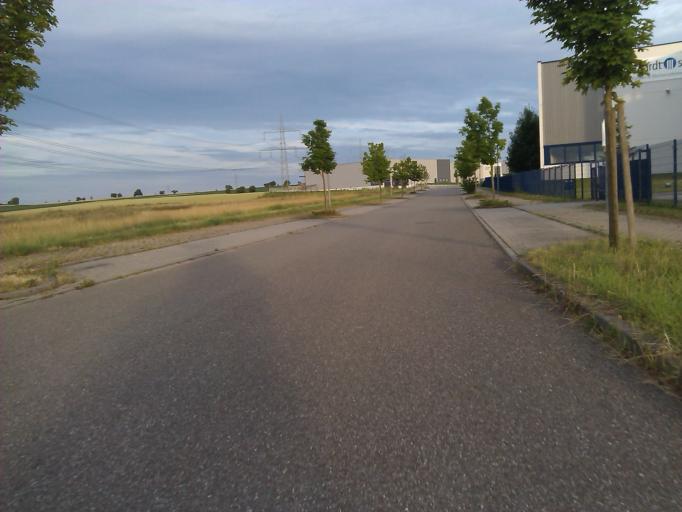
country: DE
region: Baden-Wuerttemberg
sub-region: Regierungsbezirk Stuttgart
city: Cleebronn
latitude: 49.0657
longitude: 9.0422
